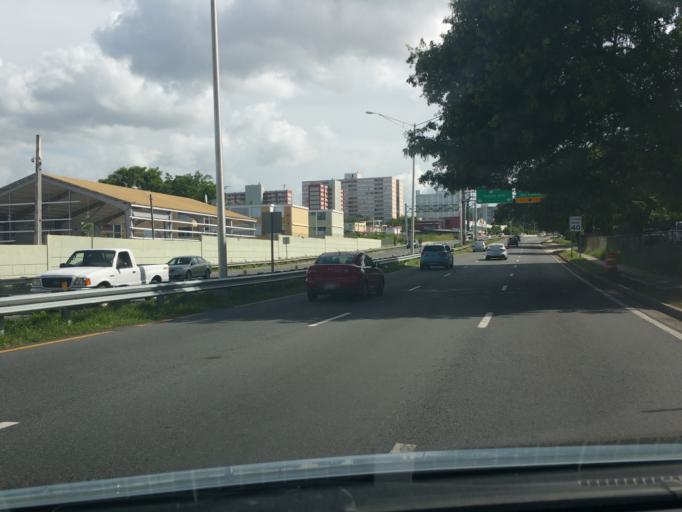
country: PR
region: Trujillo Alto
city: Trujillo Alto
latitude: 18.4045
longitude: -66.0313
